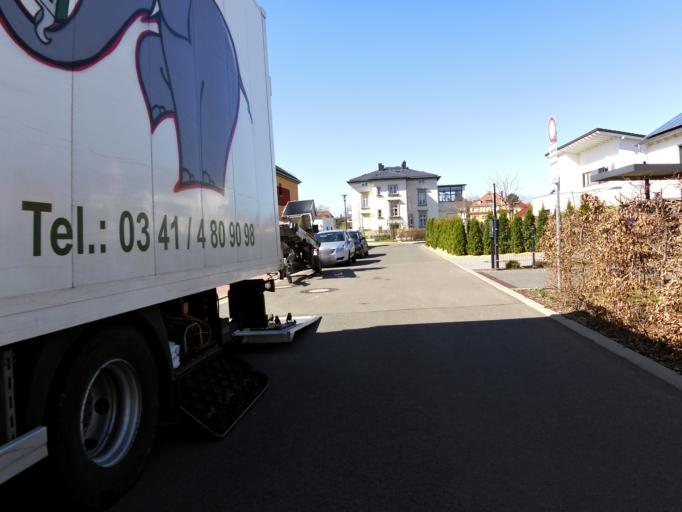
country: DE
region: Saxony
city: Markkleeberg
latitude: 51.2789
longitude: 12.3988
